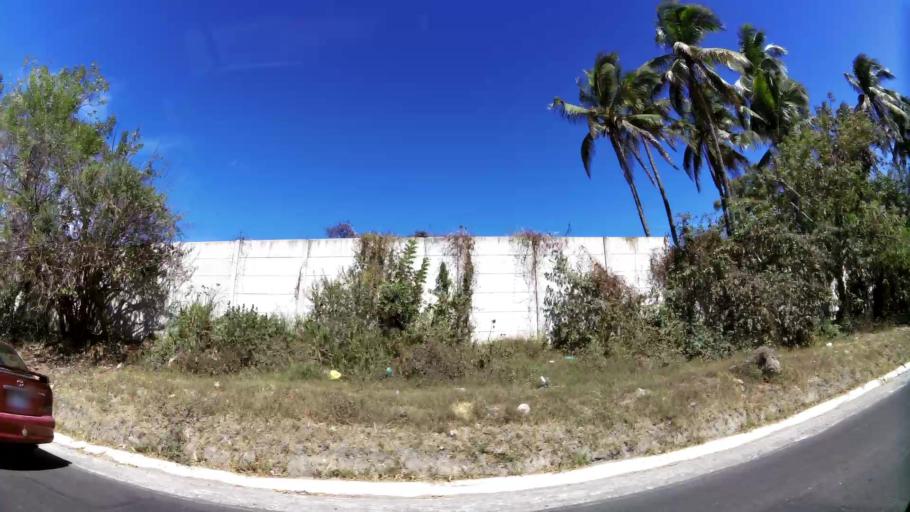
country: SV
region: San Salvador
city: Apopa
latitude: 13.8032
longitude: -89.1855
